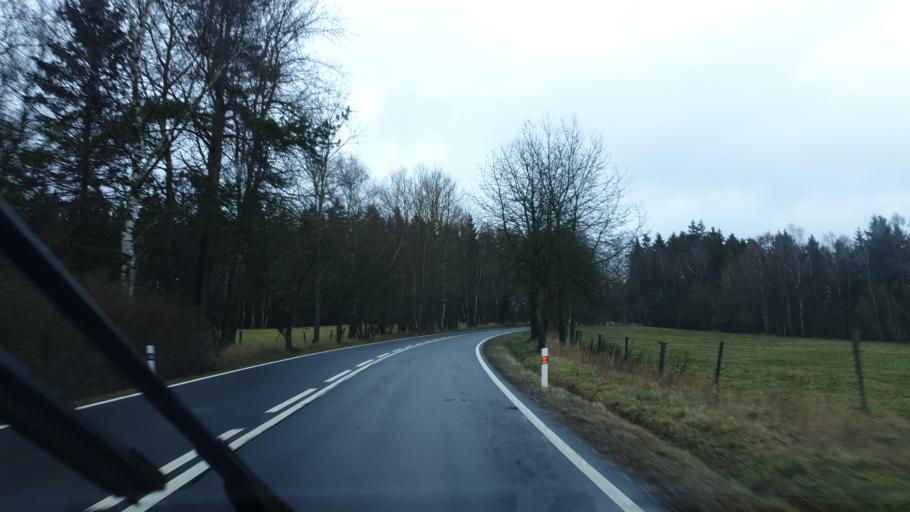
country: CZ
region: Karlovarsky
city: As
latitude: 50.2580
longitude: 12.1792
